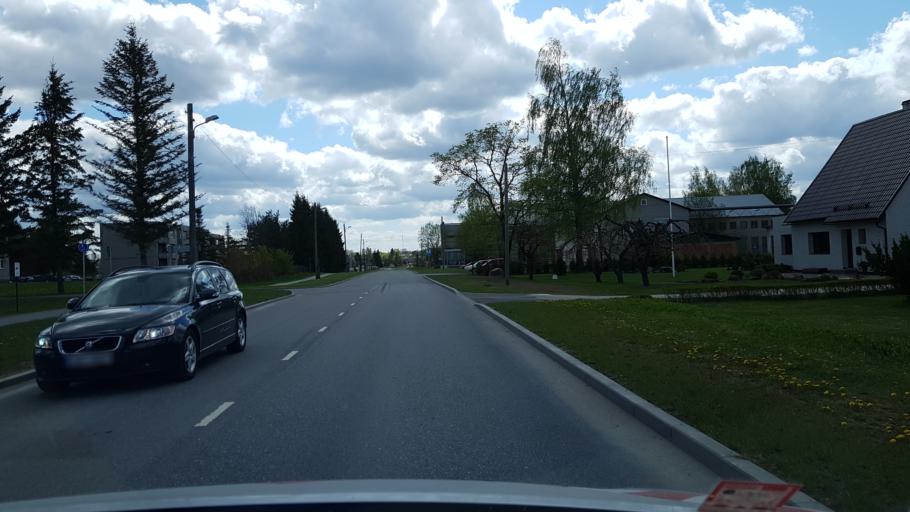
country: EE
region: Jogevamaa
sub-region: Poltsamaa linn
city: Poltsamaa
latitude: 58.6662
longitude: 25.9677
